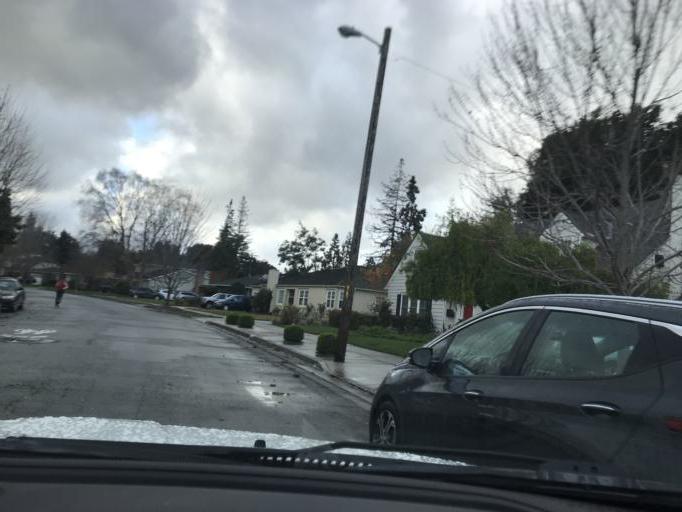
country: US
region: California
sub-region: Santa Clara County
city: Buena Vista
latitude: 37.3064
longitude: -121.9110
